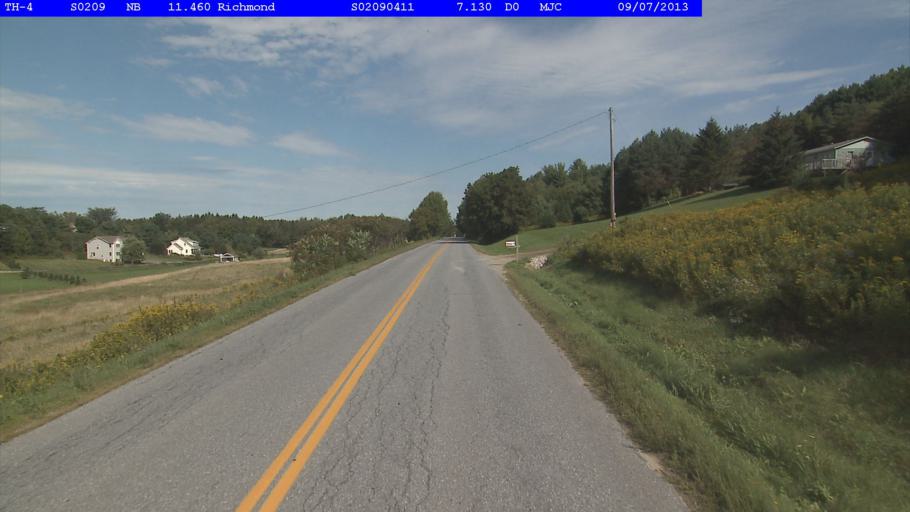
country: US
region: Vermont
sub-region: Chittenden County
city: Jericho
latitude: 44.4266
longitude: -72.9814
